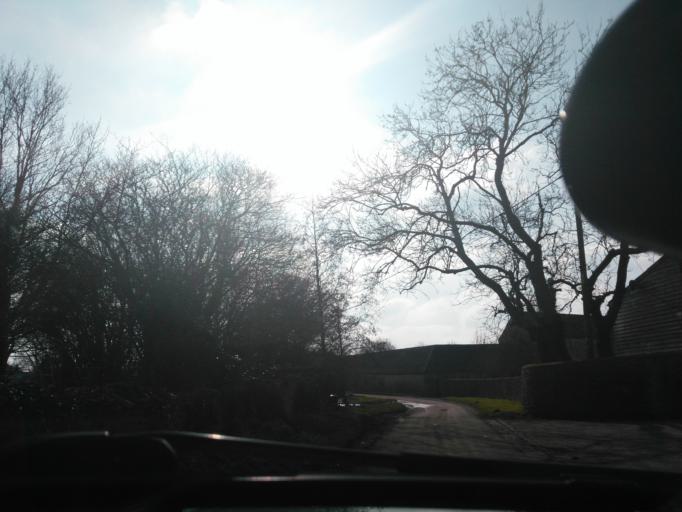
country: GB
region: England
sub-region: Gloucestershire
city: Tetbury
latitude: 51.6540
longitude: -2.0999
